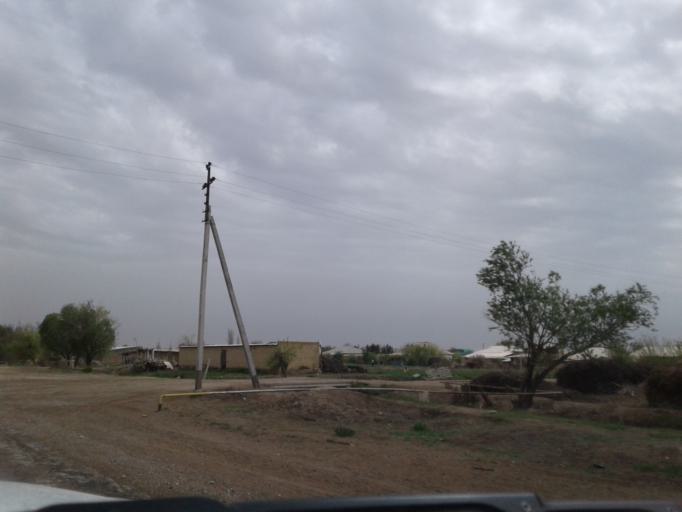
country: TM
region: Lebap
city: Atamyrat
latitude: 38.1705
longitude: 64.9093
